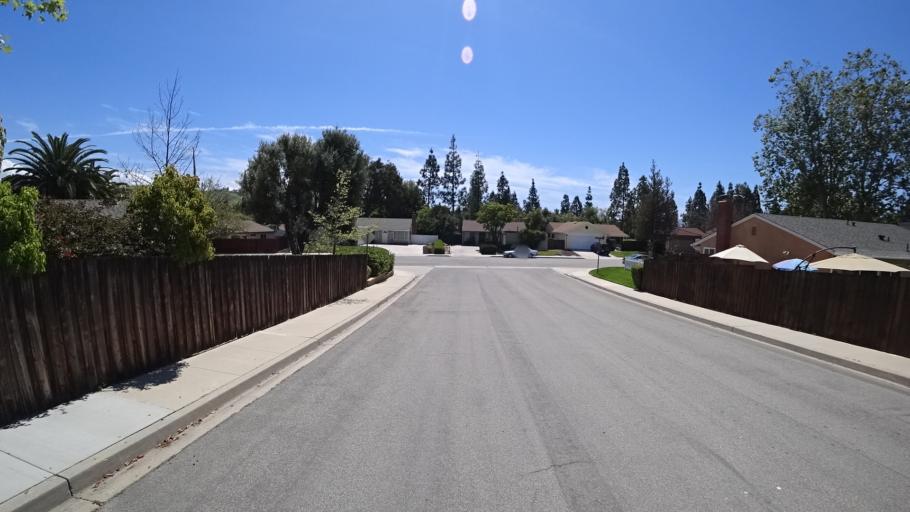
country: US
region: California
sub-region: Ventura County
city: Thousand Oaks
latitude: 34.2135
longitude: -118.8458
